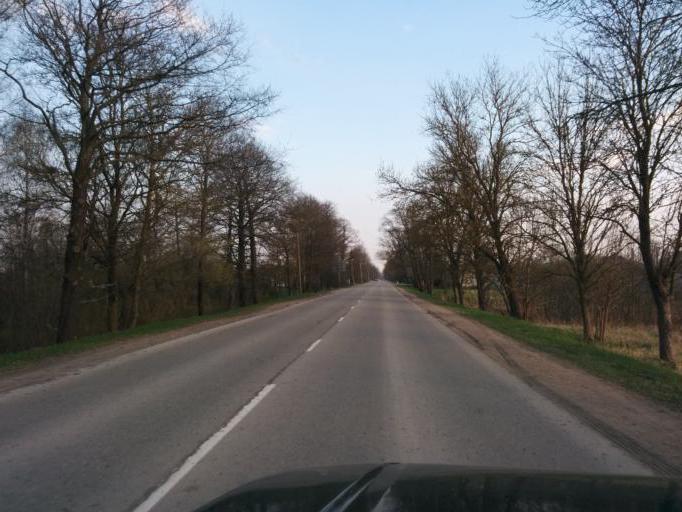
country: LV
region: Jelgava
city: Jelgava
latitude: 56.6688
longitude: 23.7315
